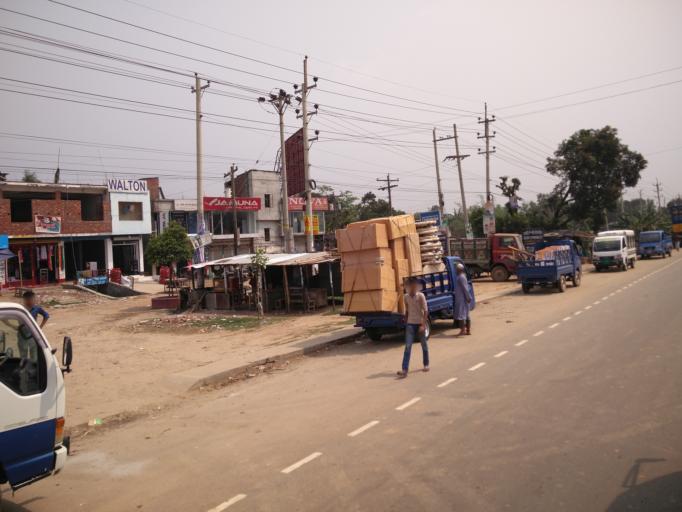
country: BD
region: Dhaka
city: Gafargaon
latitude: 24.4450
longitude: 90.3834
